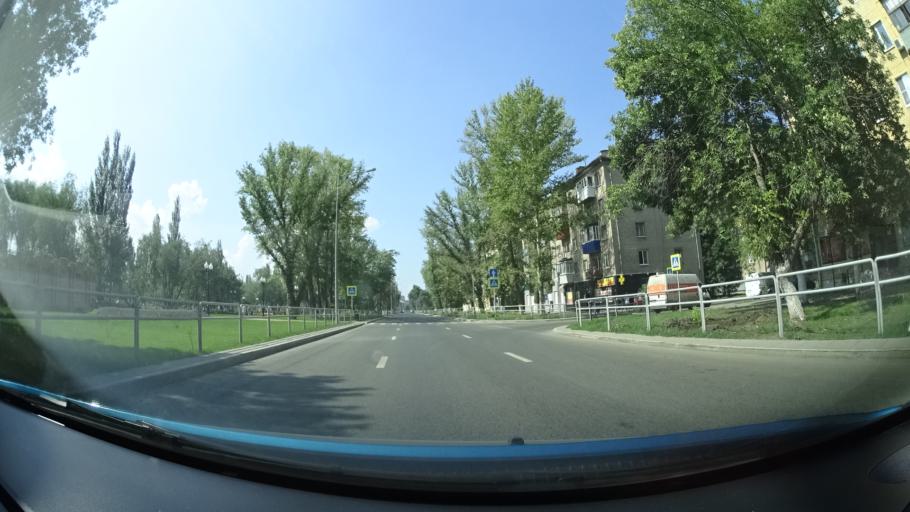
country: RU
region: Samara
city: Samara
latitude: 53.2068
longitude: 50.1667
